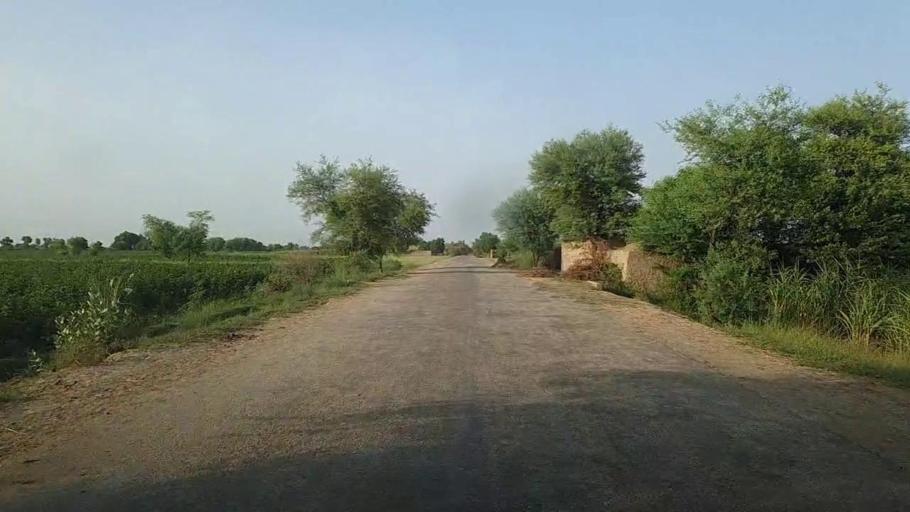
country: PK
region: Sindh
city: Ubauro
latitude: 28.1237
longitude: 69.8281
